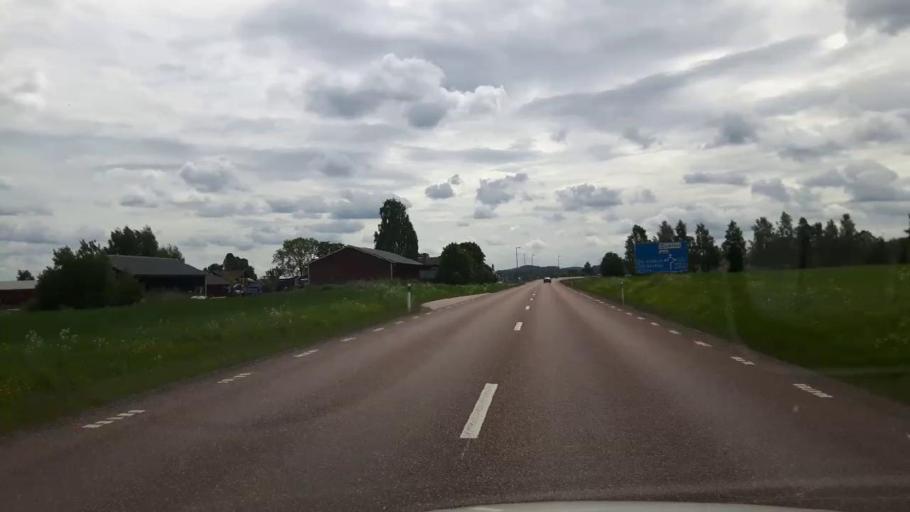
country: SE
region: Dalarna
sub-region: Hedemora Kommun
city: Hedemora
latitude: 60.3004
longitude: 15.9787
